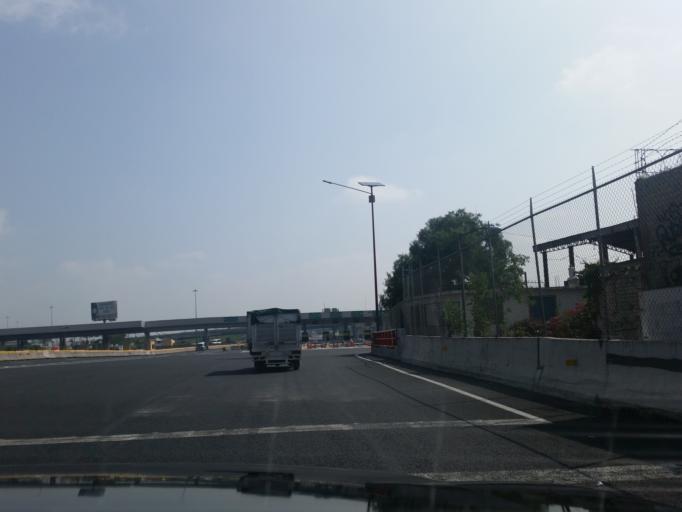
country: MX
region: Mexico
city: Ecatepec
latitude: 19.6011
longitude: -99.0387
